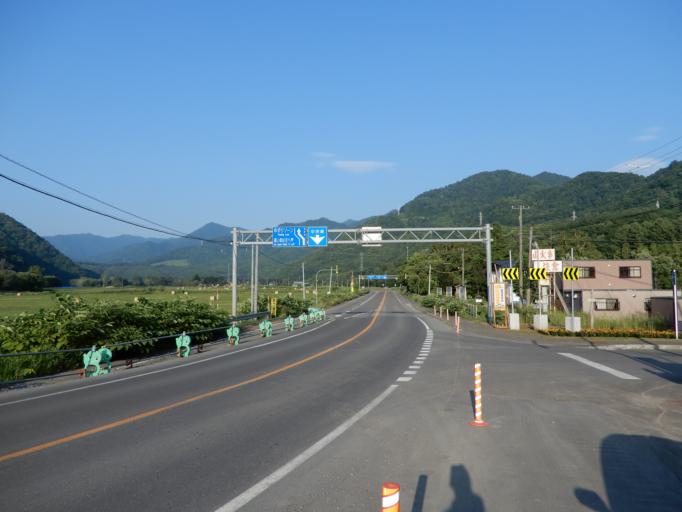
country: JP
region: Hokkaido
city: Shimo-furano
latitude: 42.8918
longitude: 142.5366
